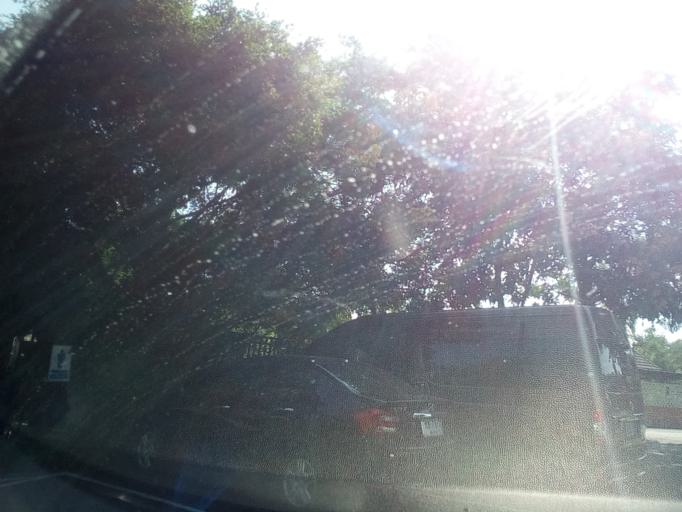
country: TH
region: Chiang Mai
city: Chiang Mai
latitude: 18.8051
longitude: 98.9458
